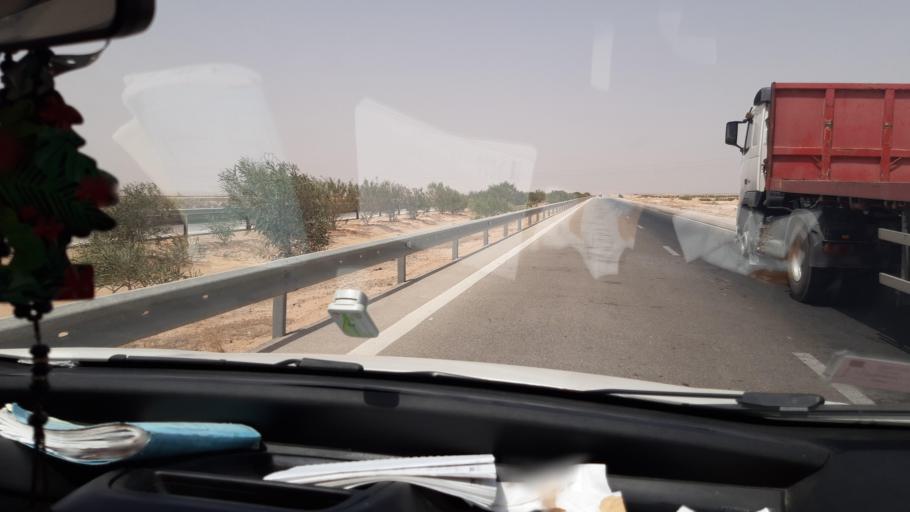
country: TN
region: Qabis
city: Gabes
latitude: 33.9393
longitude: 9.9619
